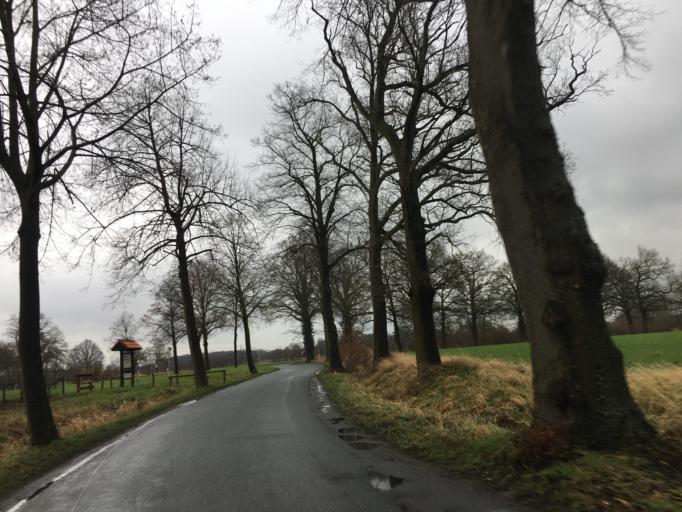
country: DE
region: North Rhine-Westphalia
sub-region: Regierungsbezirk Munster
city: Nordwalde
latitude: 52.0941
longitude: 7.4885
